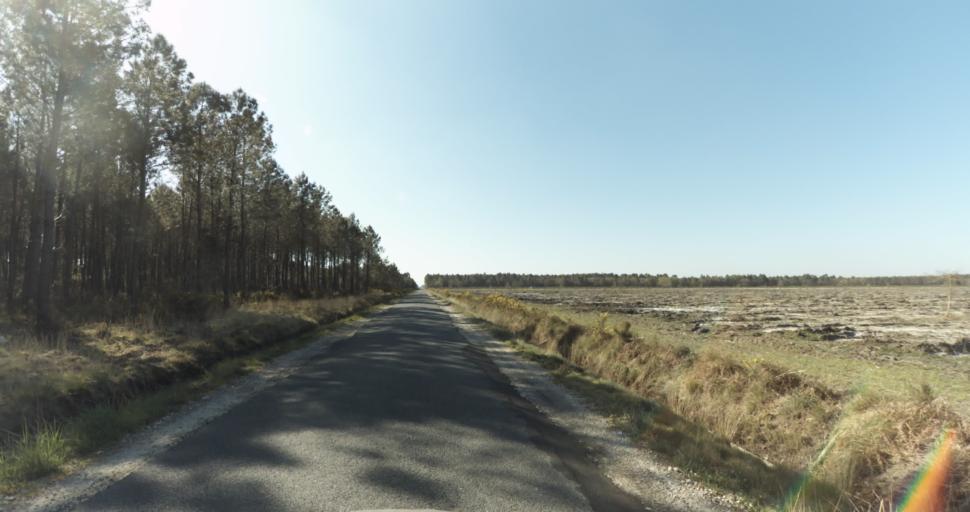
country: FR
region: Aquitaine
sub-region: Departement de la Gironde
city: Martignas-sur-Jalle
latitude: 44.7913
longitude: -0.8643
